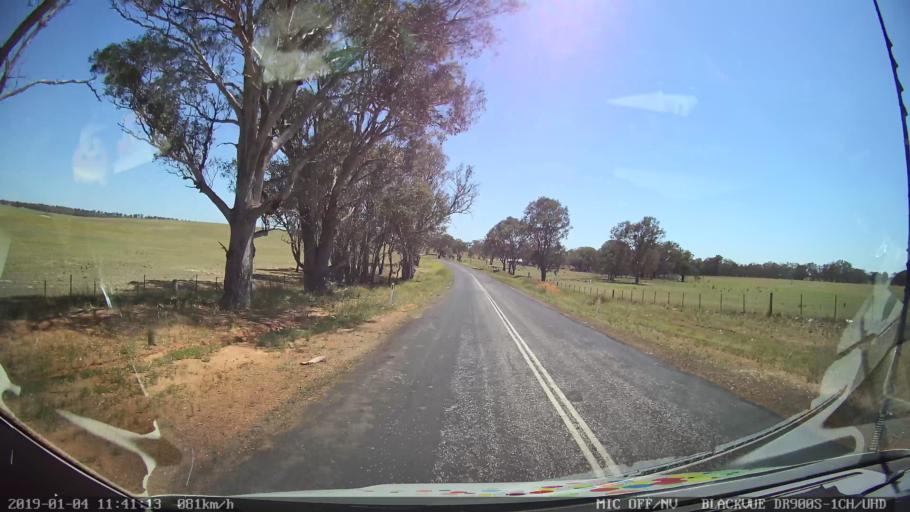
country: AU
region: New South Wales
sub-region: Cabonne
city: Molong
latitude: -32.9962
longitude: 148.7871
